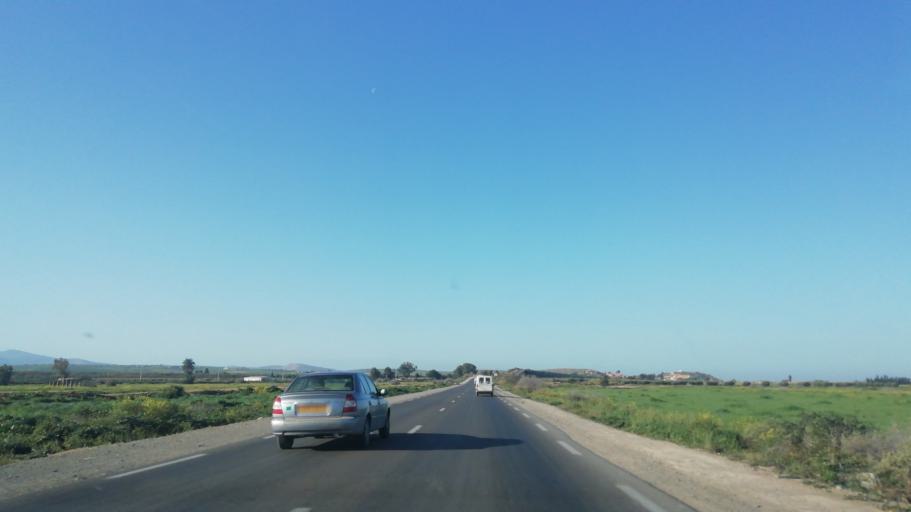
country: DZ
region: Mascara
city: Mascara
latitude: 35.6552
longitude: 0.1906
